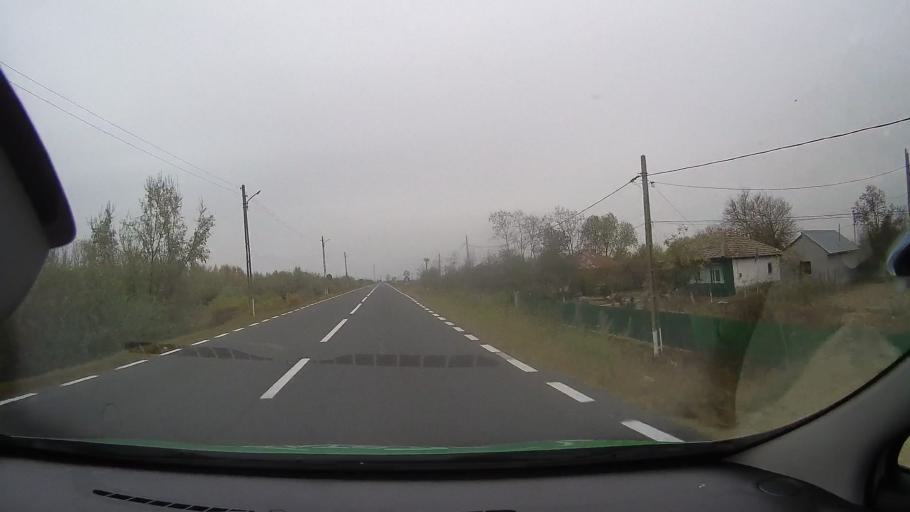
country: RO
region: Ialomita
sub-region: Comuna Giurgeni
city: Giurgeni
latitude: 44.7342
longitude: 27.8549
